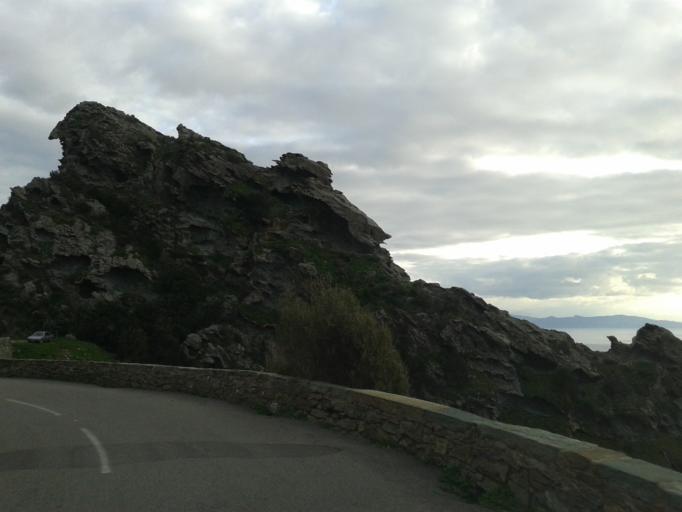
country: FR
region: Corsica
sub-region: Departement de la Haute-Corse
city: Brando
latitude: 42.8777
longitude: 9.3304
